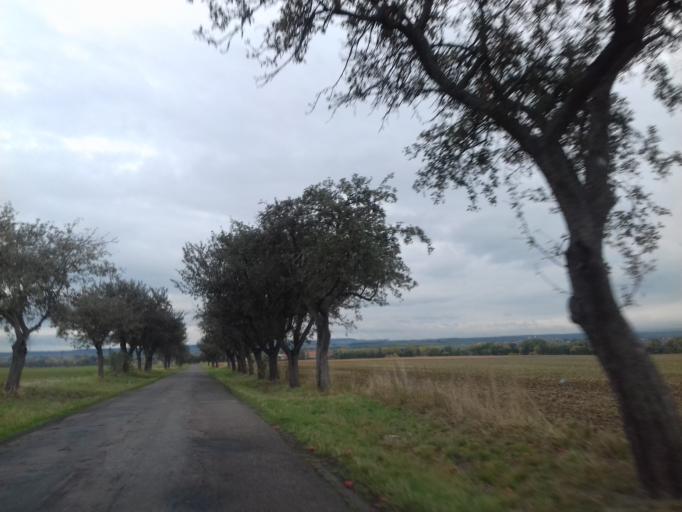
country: CZ
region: Pardubicky
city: Hrochuv Tynec
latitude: 49.9231
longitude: 15.8876
